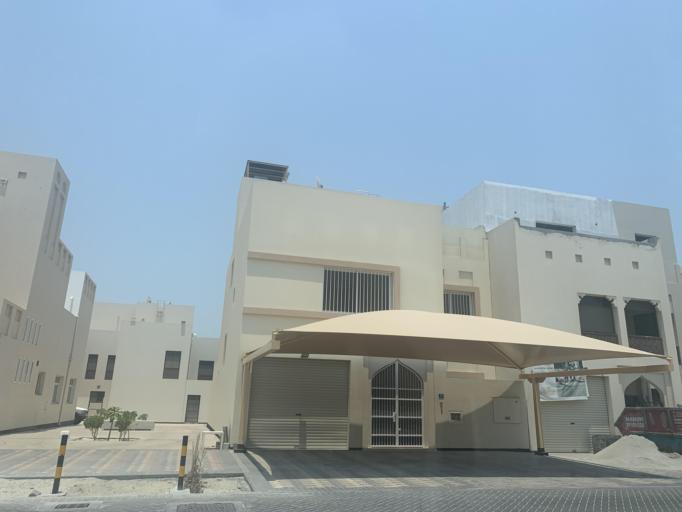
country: BH
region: Muharraq
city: Al Hadd
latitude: 26.2336
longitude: 50.6713
